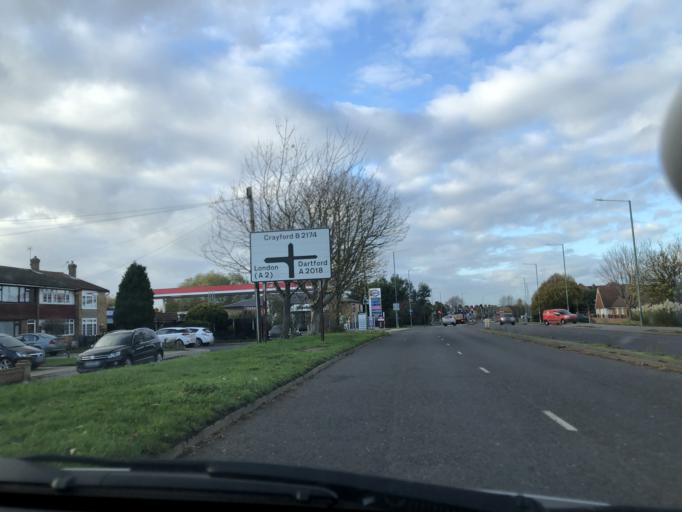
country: GB
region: England
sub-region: Kent
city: Dartford
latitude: 51.4402
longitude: 0.1977
